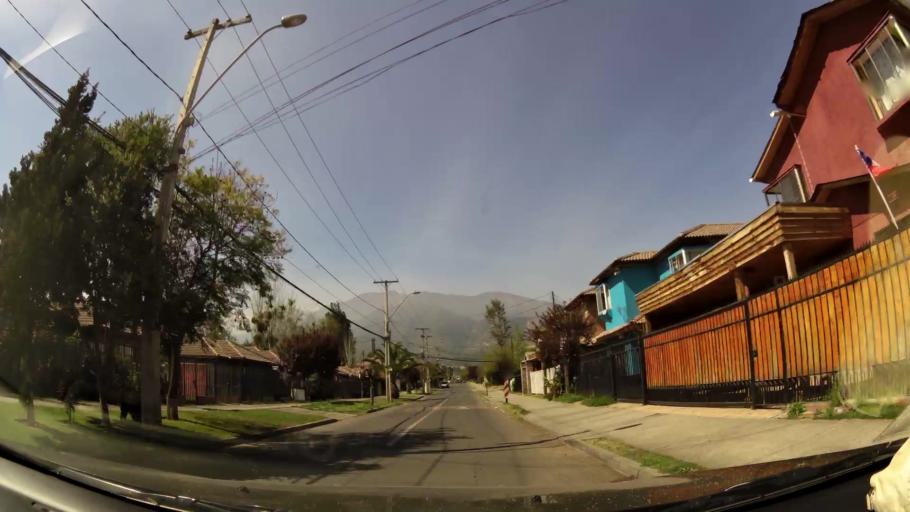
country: CL
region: Santiago Metropolitan
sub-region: Provincia de Cordillera
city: Puente Alto
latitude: -33.5618
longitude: -70.5622
